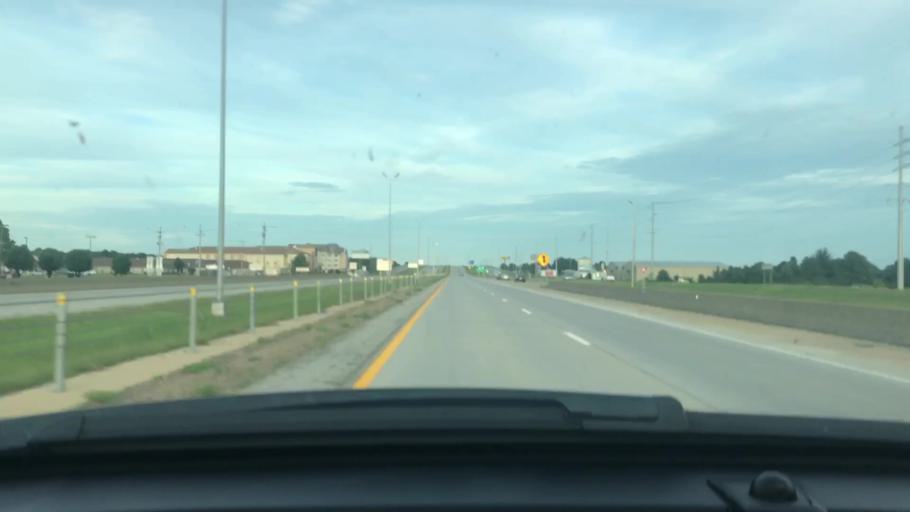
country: US
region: Arkansas
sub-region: Craighead County
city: Jonesboro
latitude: 35.8070
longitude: -90.6673
